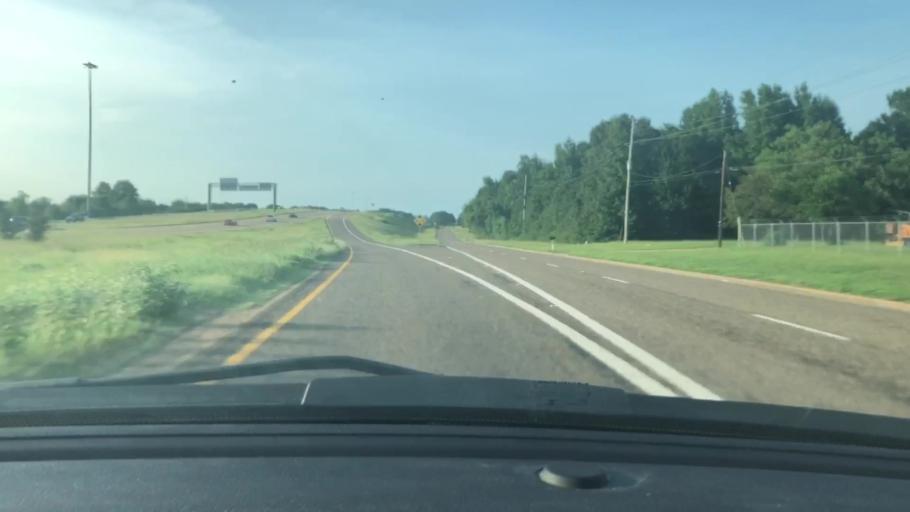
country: US
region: Texas
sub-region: Bowie County
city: Wake Village
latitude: 33.3981
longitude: -94.0972
